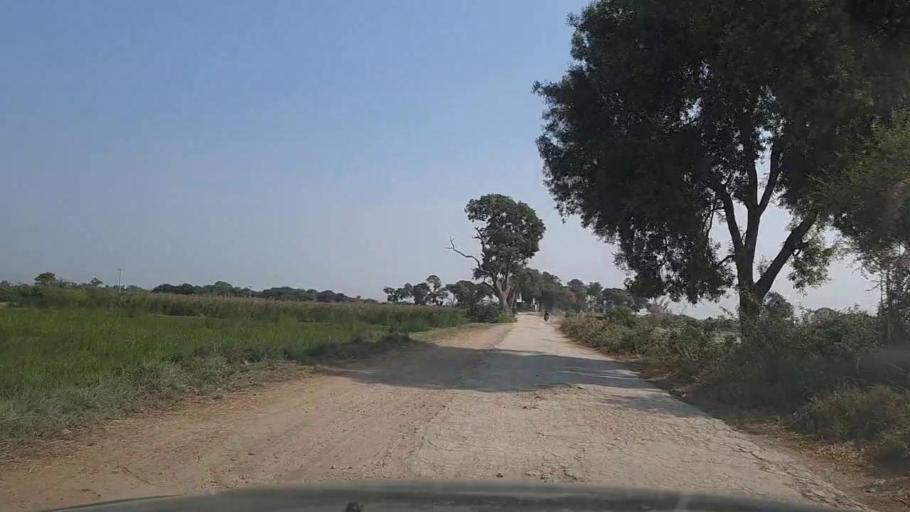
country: PK
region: Sindh
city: Thatta
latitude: 24.5799
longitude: 67.8960
